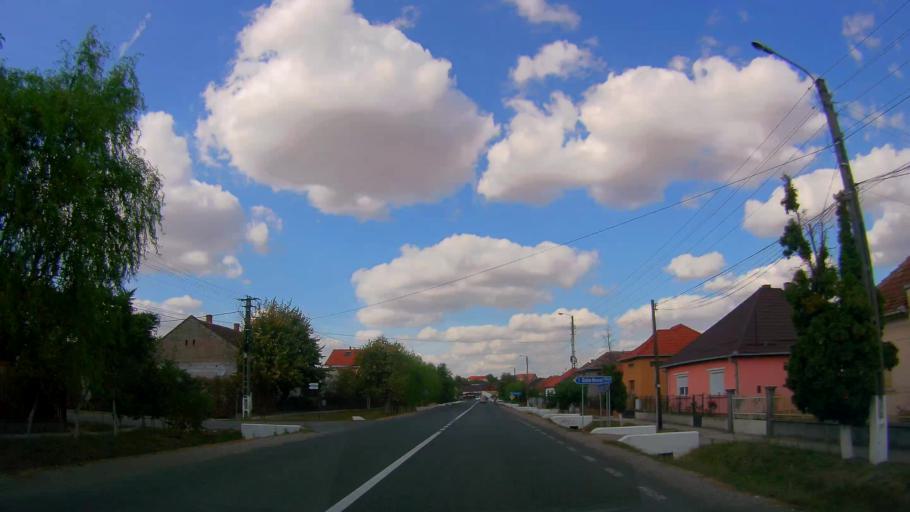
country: RO
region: Satu Mare
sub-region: Oras Ardud
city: Ardud
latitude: 47.6476
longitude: 22.8914
